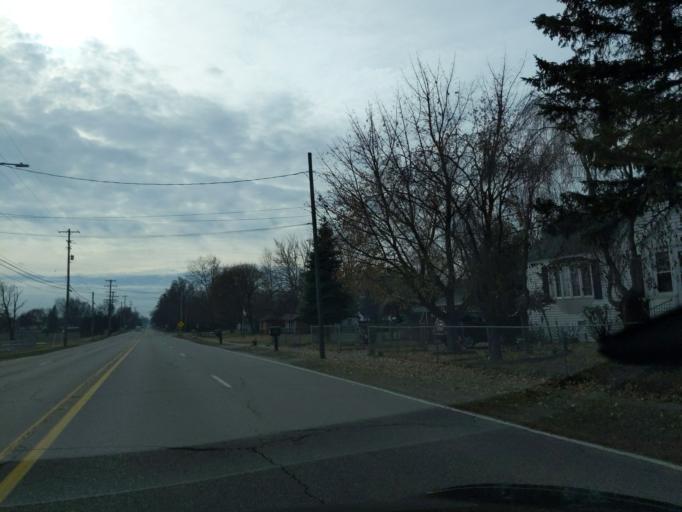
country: US
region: Michigan
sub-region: Ingham County
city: Holt
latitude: 42.6342
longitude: -84.5234
